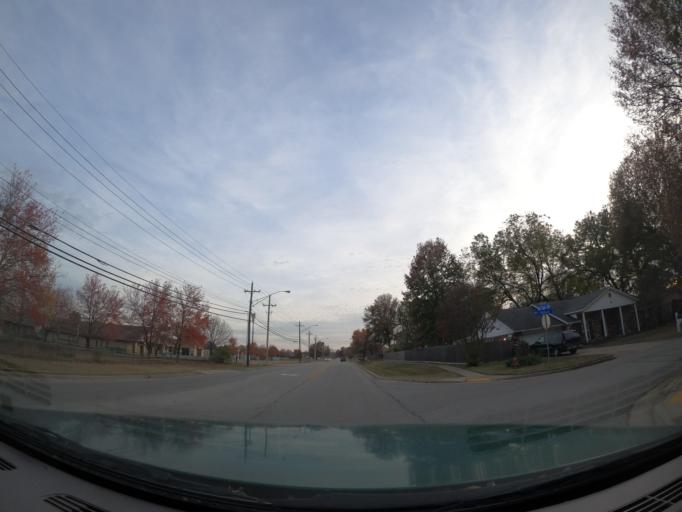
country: US
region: Oklahoma
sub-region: Tulsa County
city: Broken Arrow
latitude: 35.9778
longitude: -95.7974
